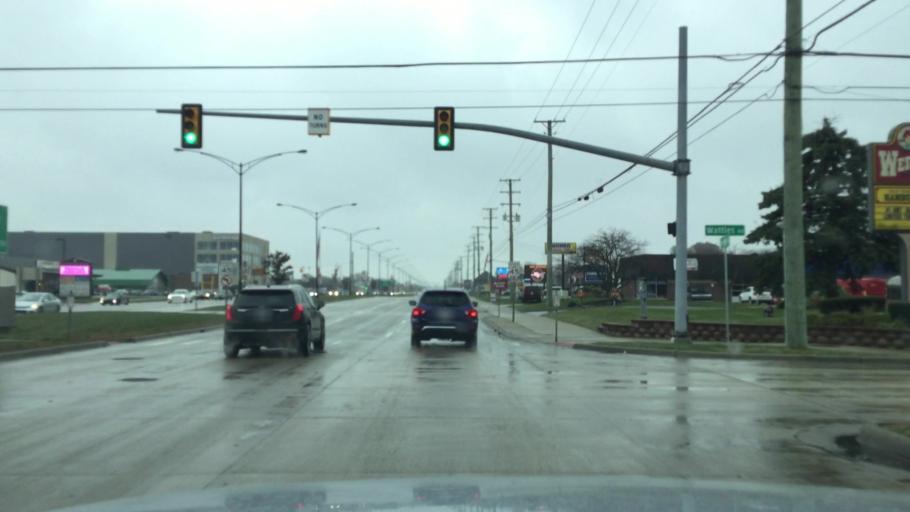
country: US
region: Michigan
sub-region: Oakland County
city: Troy
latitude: 42.5777
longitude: -83.1286
